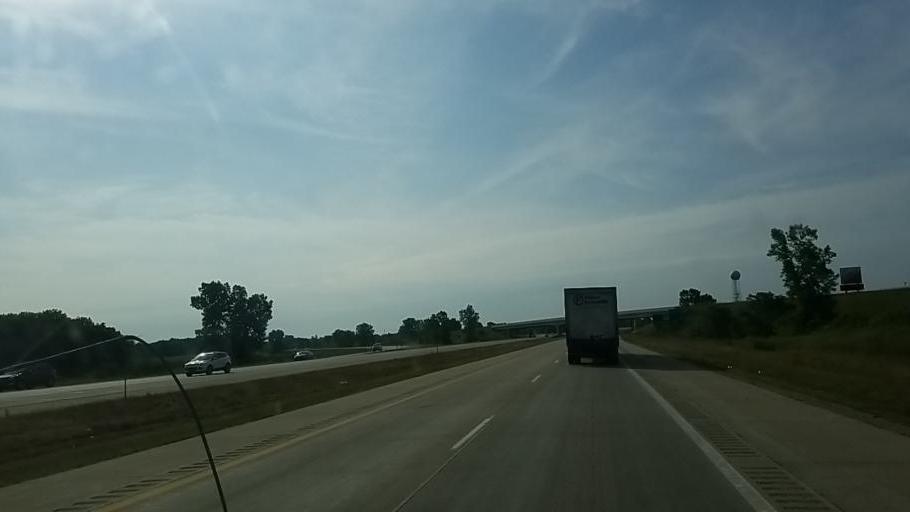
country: US
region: Michigan
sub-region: Clinton County
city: Wacousta
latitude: 42.7914
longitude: -84.6796
